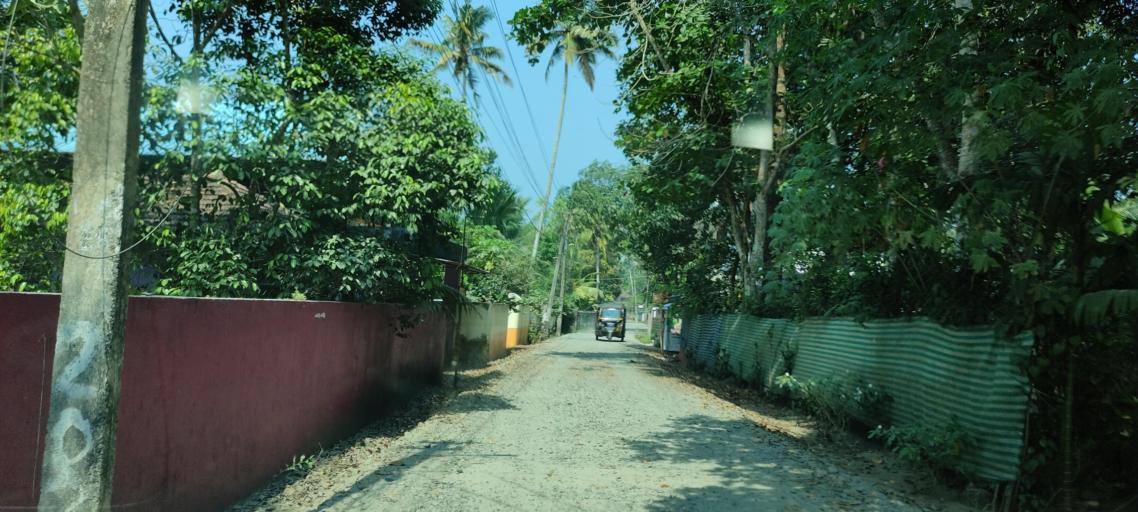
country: IN
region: Kerala
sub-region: Alappuzha
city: Alleppey
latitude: 9.5331
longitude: 76.3199
